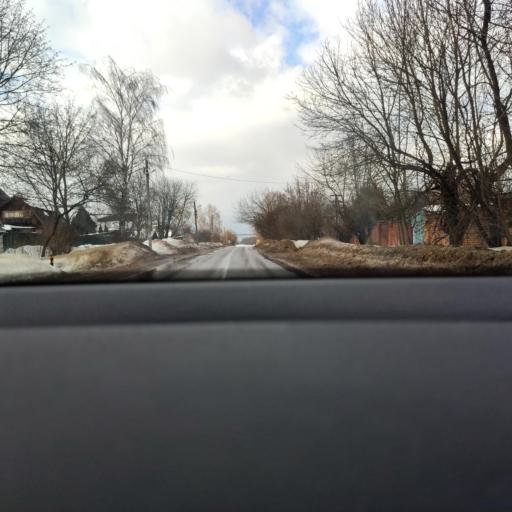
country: RU
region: Moskovskaya
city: Istra
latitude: 56.0269
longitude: 36.8075
